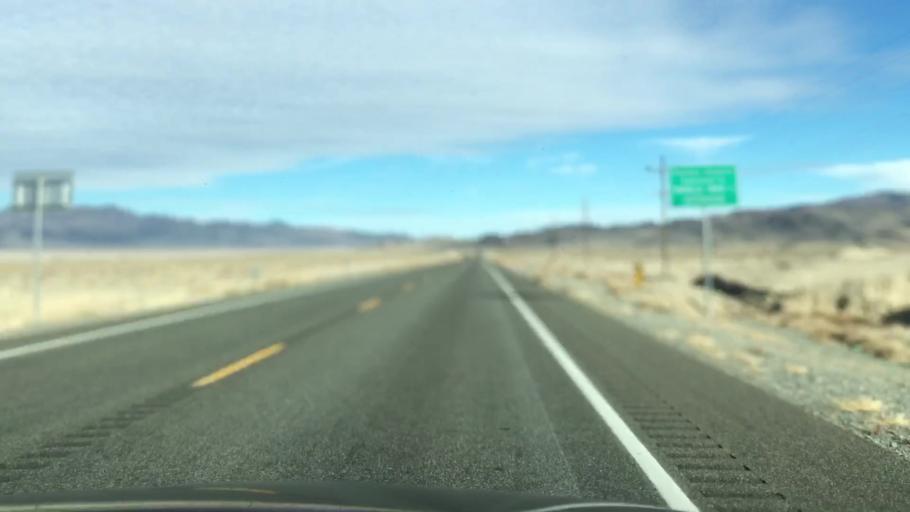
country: US
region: Nevada
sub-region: Mineral County
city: Hawthorne
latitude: 38.5272
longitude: -118.5632
